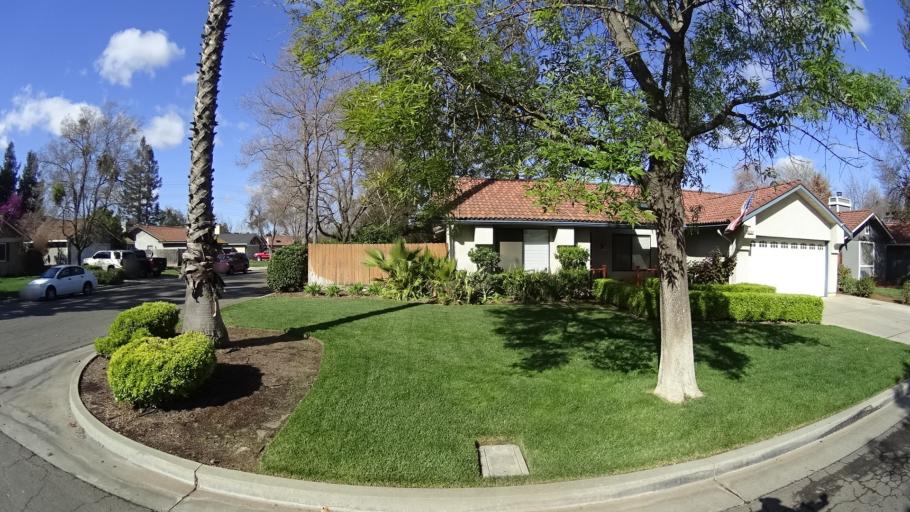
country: US
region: California
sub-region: Fresno County
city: West Park
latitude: 36.8242
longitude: -119.8812
